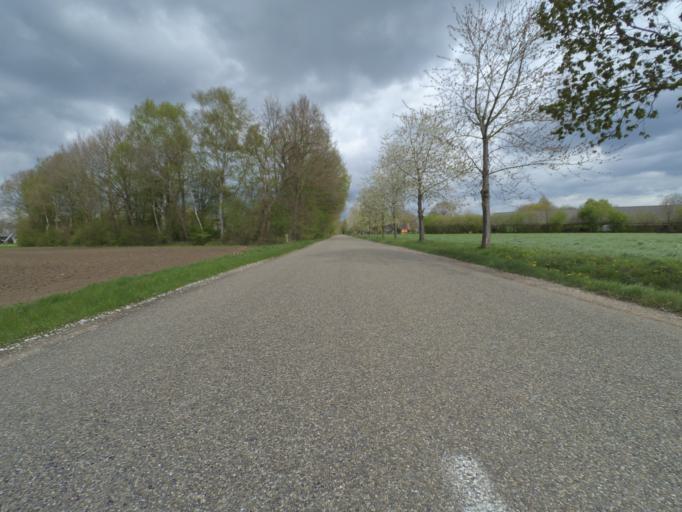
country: NL
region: Gelderland
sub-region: Gemeente Ede
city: Wekerom
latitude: 52.0986
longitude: 5.7358
